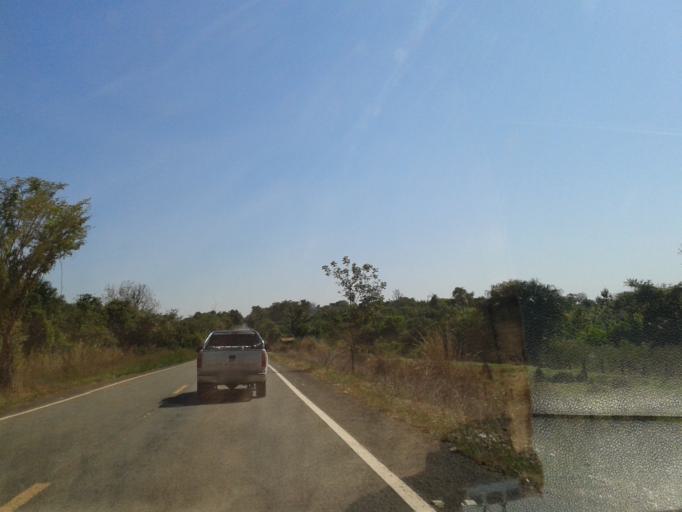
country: BR
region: Goias
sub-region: Sao Miguel Do Araguaia
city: Sao Miguel do Araguaia
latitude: -13.8828
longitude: -50.3300
